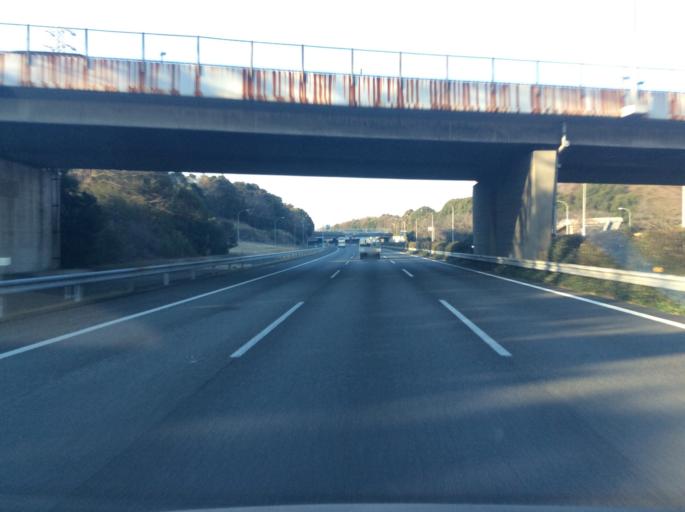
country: JP
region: Chiba
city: Nagareyama
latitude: 35.9092
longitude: 139.9354
